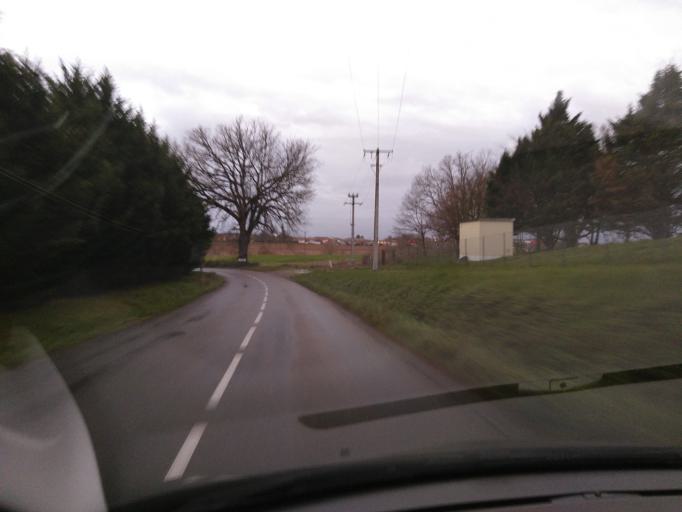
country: FR
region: Midi-Pyrenees
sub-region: Departement de la Haute-Garonne
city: Seilh
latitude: 43.6826
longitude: 1.3405
